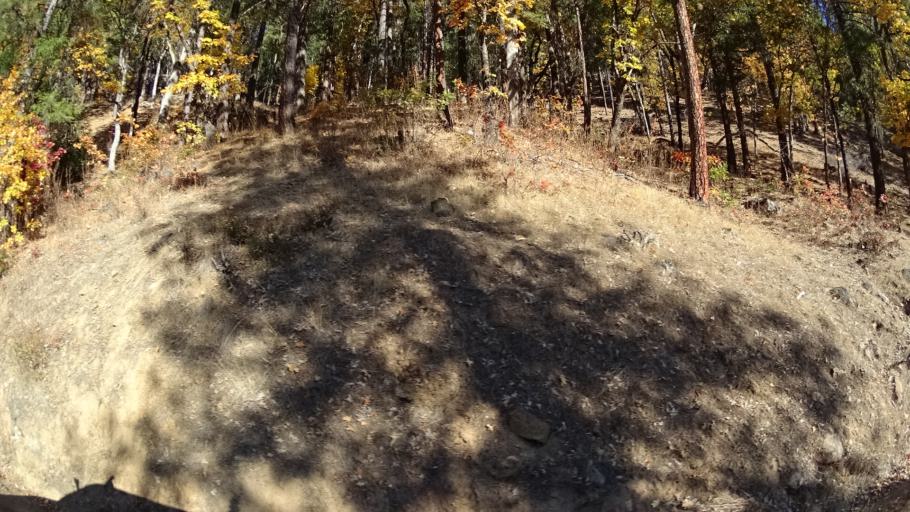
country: US
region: California
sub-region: Siskiyou County
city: Happy Camp
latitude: 41.6404
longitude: -123.0622
